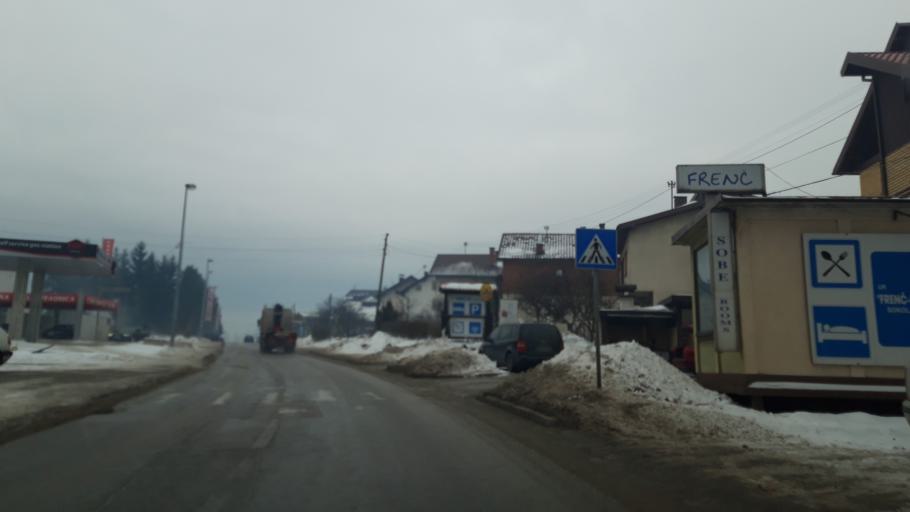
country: BA
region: Republika Srpska
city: Sokolac
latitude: 43.9359
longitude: 18.7924
